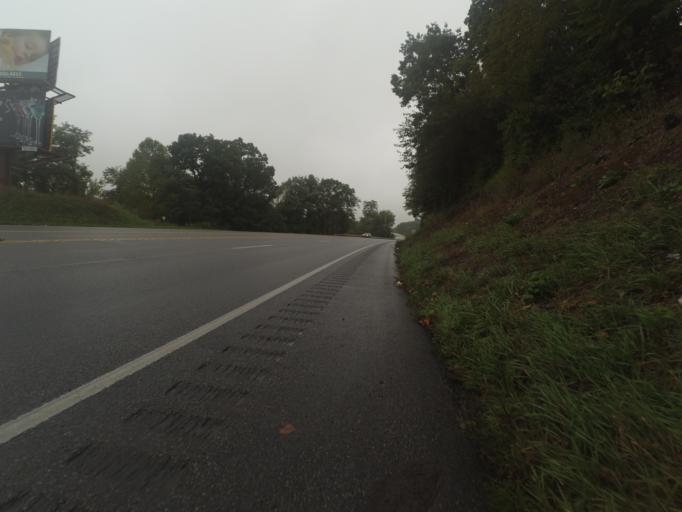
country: US
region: Pennsylvania
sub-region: Huntingdon County
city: McConnellstown
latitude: 40.5002
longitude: -78.0647
